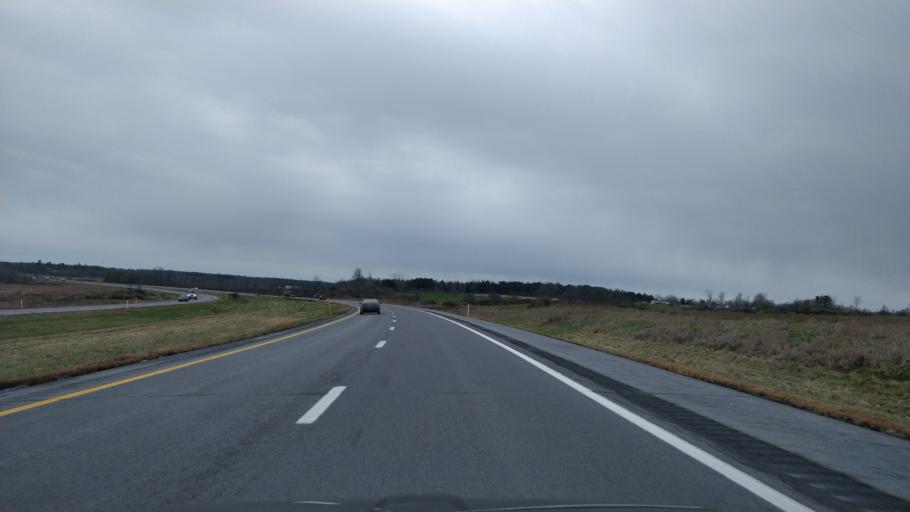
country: US
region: New York
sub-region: Jefferson County
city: Calcium
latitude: 44.1513
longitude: -75.8844
